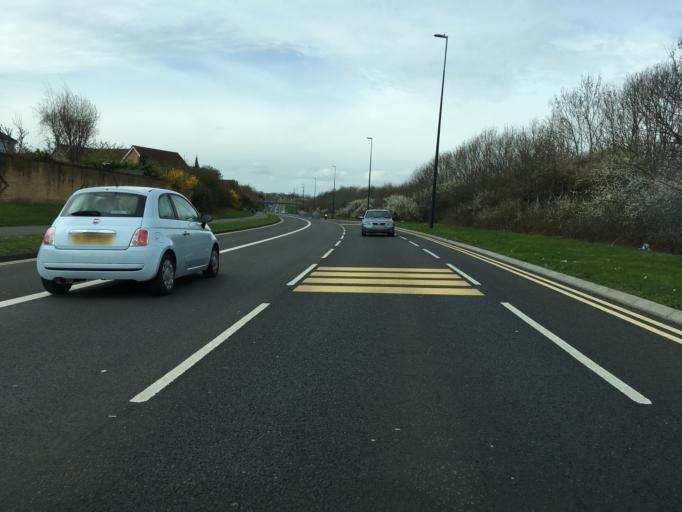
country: GB
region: England
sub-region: South Gloucestershire
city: Stoke Gifford
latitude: 51.5388
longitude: -2.5498
